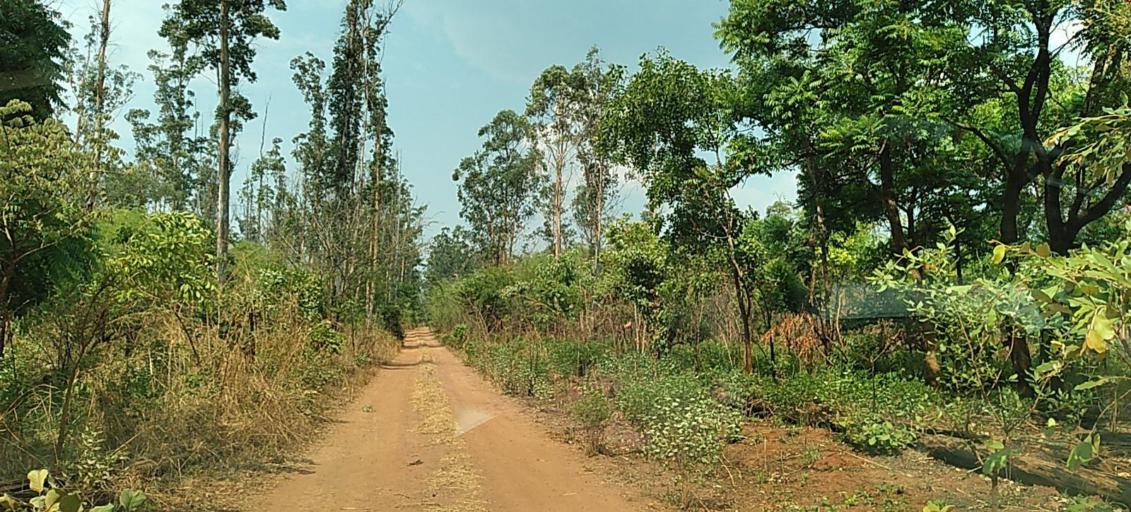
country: ZM
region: Copperbelt
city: Chingola
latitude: -12.7406
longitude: 27.7512
